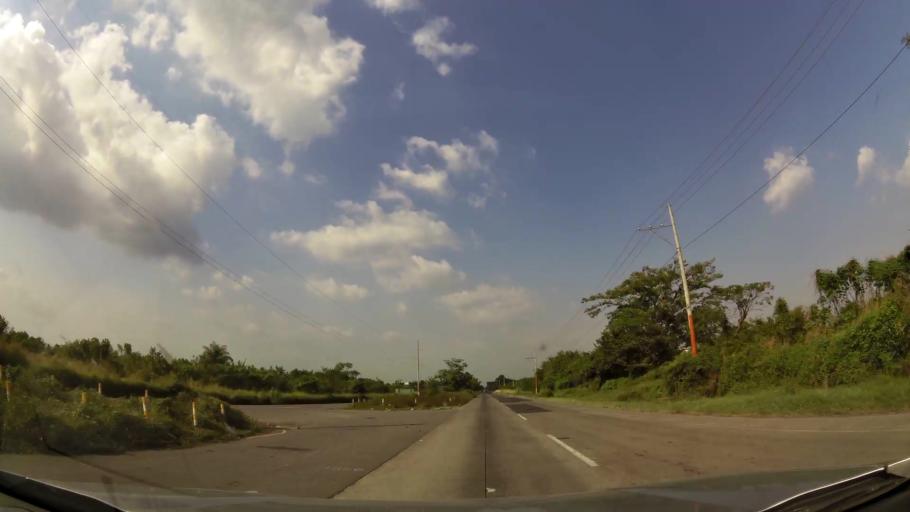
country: GT
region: Escuintla
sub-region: Municipio de Masagua
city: Masagua
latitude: 14.0950
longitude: -90.7794
